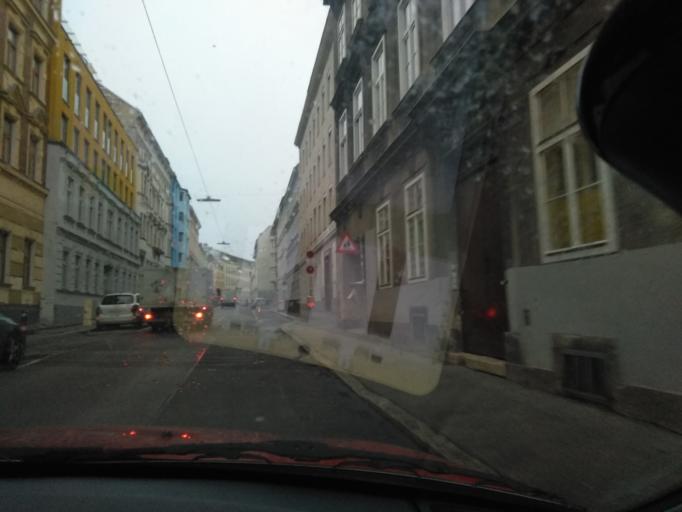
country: AT
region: Vienna
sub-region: Wien Stadt
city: Vienna
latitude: 48.2242
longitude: 16.3417
